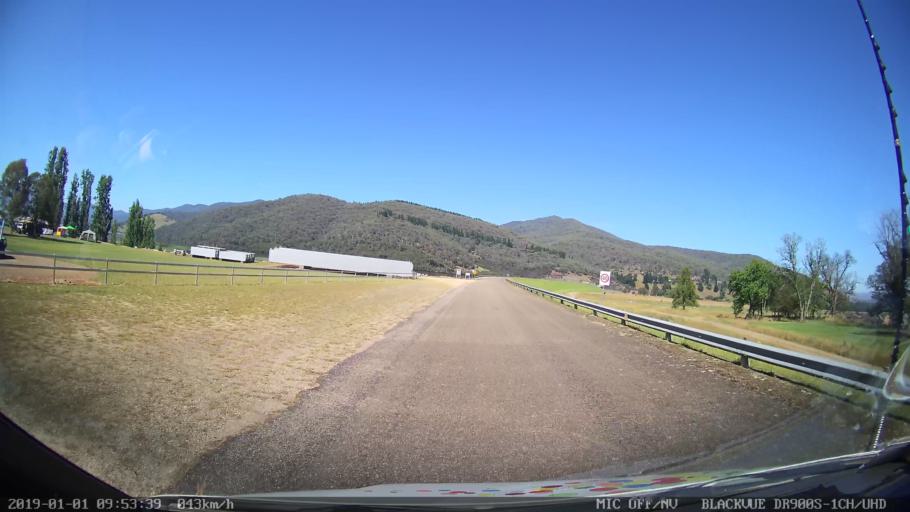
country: AU
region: New South Wales
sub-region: Snowy River
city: Jindabyne
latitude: -36.2196
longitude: 148.1189
